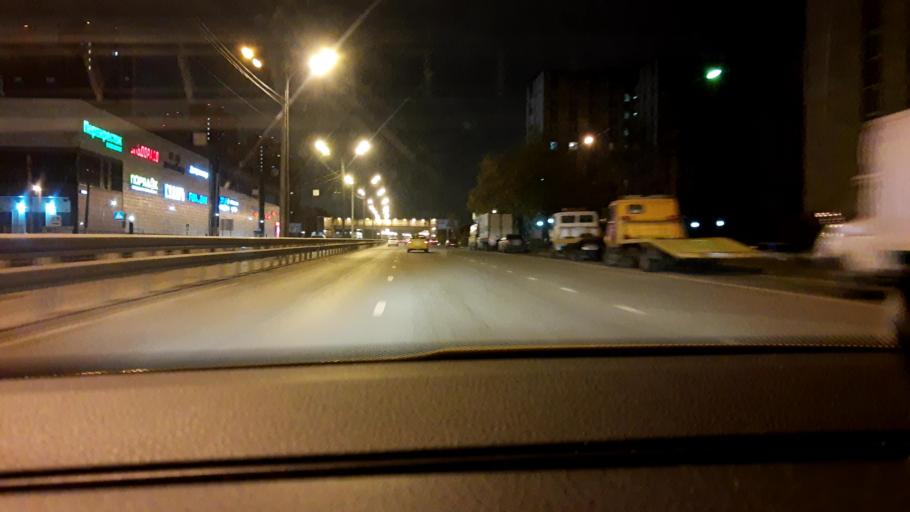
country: RU
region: Moskovskaya
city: Dolgoprudnyy
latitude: 55.9377
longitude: 37.4917
